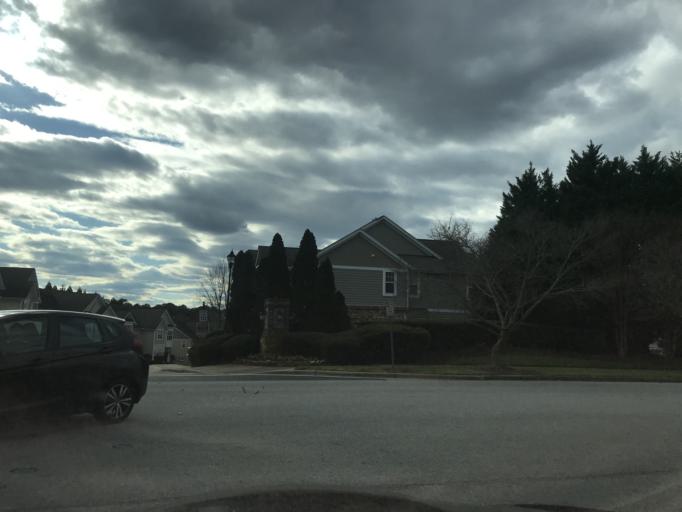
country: US
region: North Carolina
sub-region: Wake County
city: West Raleigh
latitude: 35.8599
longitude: -78.7186
